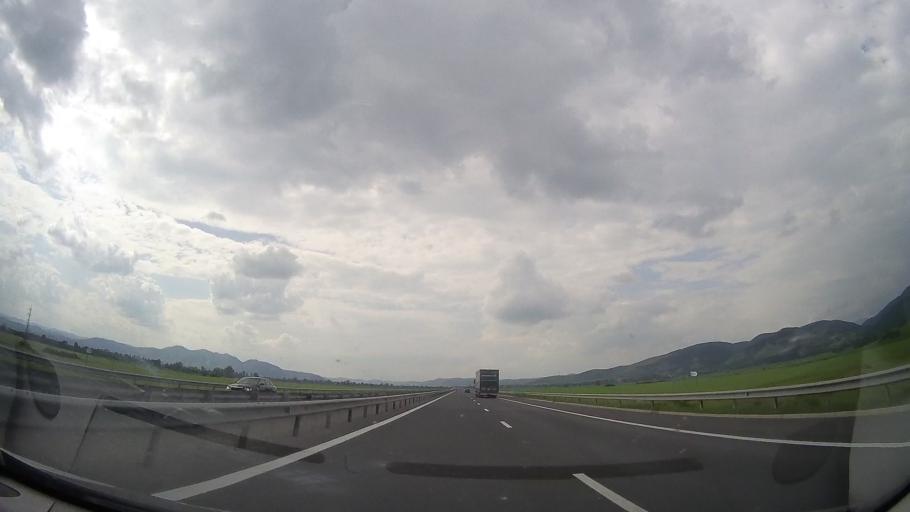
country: RO
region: Hunedoara
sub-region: Oras Simeria
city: Simeria
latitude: 45.8726
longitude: 23.0121
